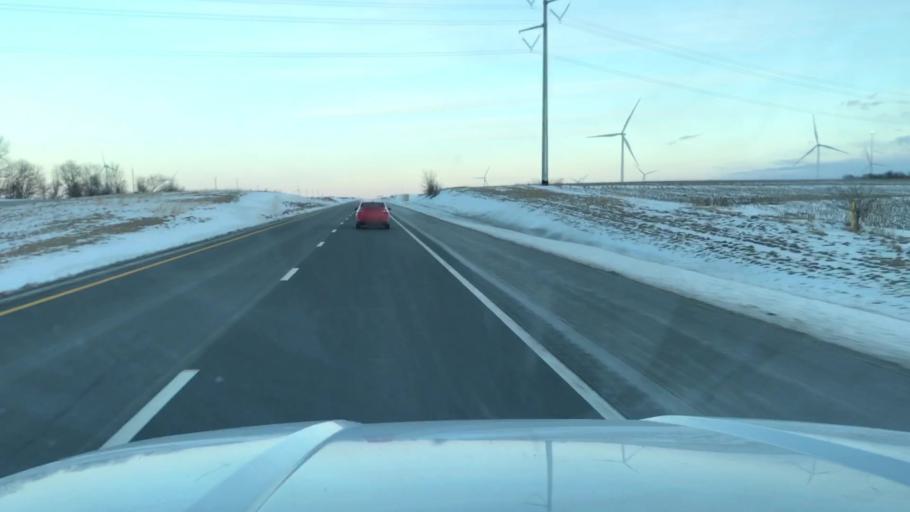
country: US
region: Missouri
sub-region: DeKalb County
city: Maysville
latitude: 39.7618
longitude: -94.4452
